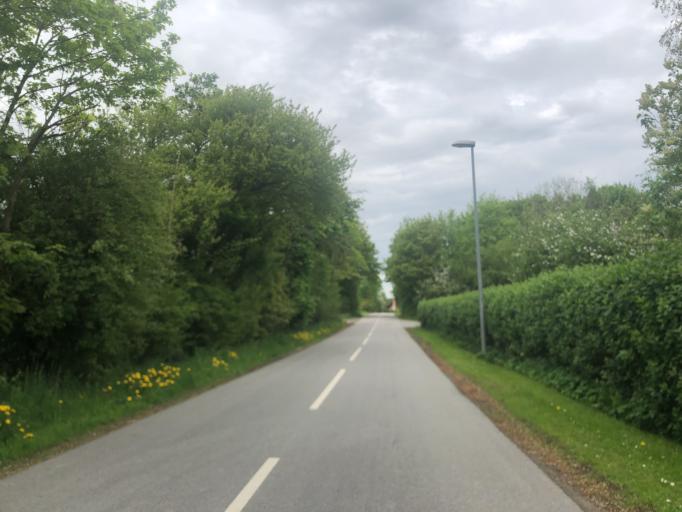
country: DK
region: Zealand
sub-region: Koge Kommune
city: Ejby
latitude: 55.4628
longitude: 12.1055
